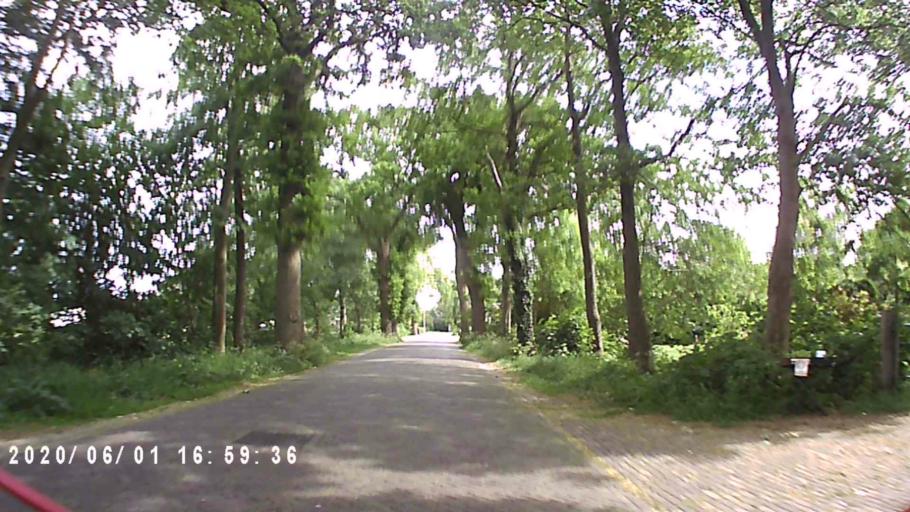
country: NL
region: Friesland
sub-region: Gemeente Tytsjerksteradiel
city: Hurdegaryp
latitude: 53.1857
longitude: 5.9284
